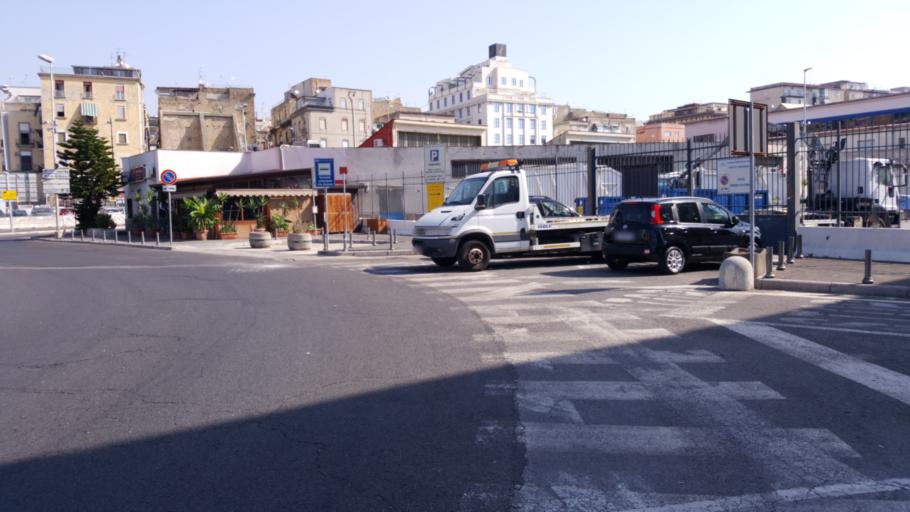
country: IT
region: Campania
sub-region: Provincia di Napoli
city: Napoli
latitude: 40.8450
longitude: 14.2633
